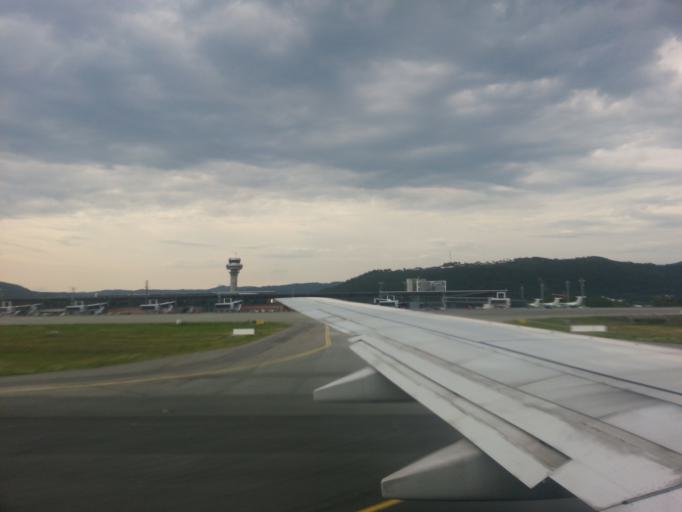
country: NO
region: Nord-Trondelag
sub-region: Stjordal
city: Stjordalshalsen
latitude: 63.4572
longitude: 10.9238
